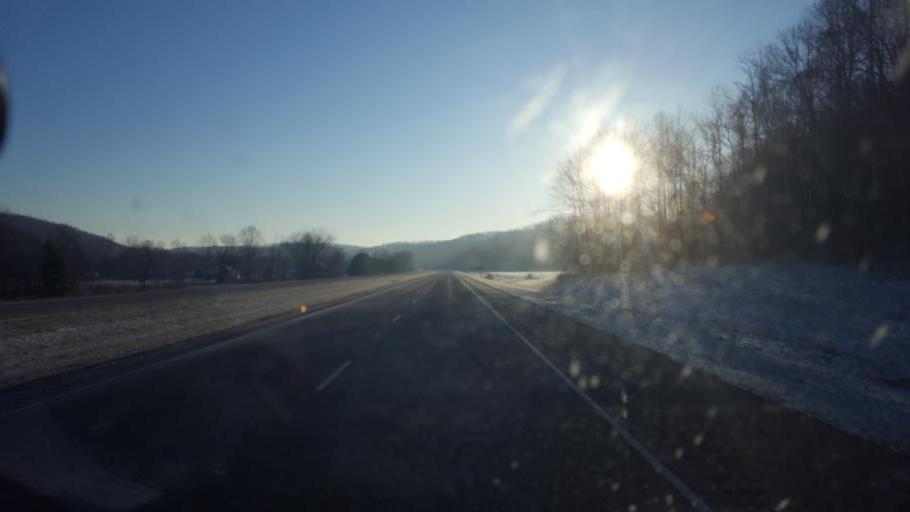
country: US
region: Ohio
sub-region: Pike County
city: Piketon
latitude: 39.0459
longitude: -83.1764
